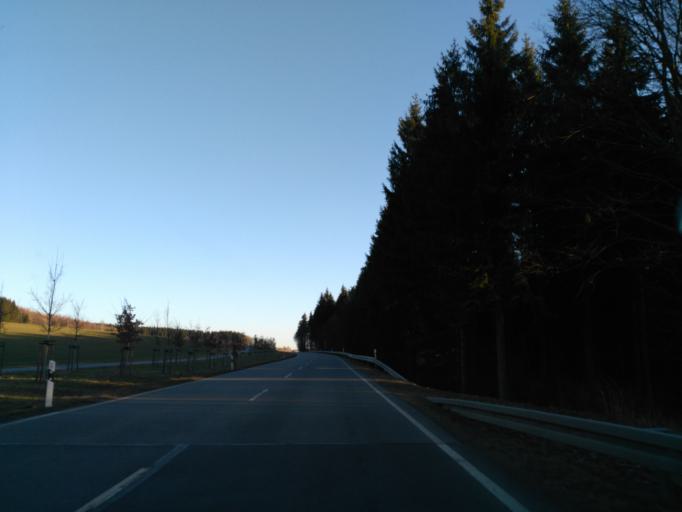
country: DE
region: Saxony
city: Konigswalde
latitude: 50.5367
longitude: 13.0239
